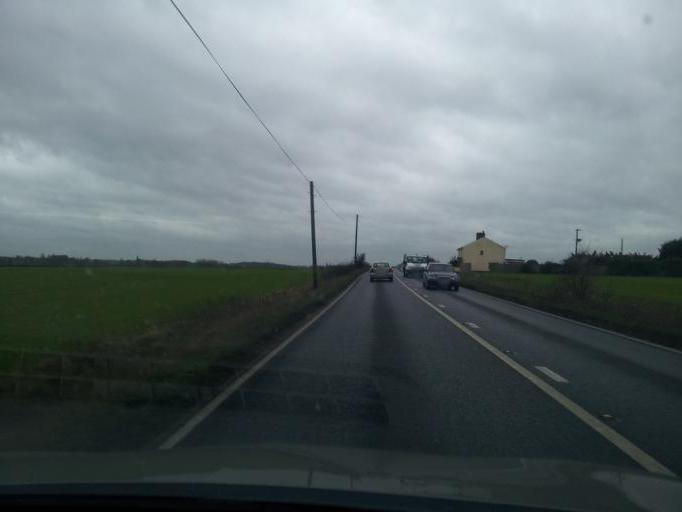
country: GB
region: England
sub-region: Suffolk
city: Thurston
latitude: 52.2806
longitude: 0.8039
